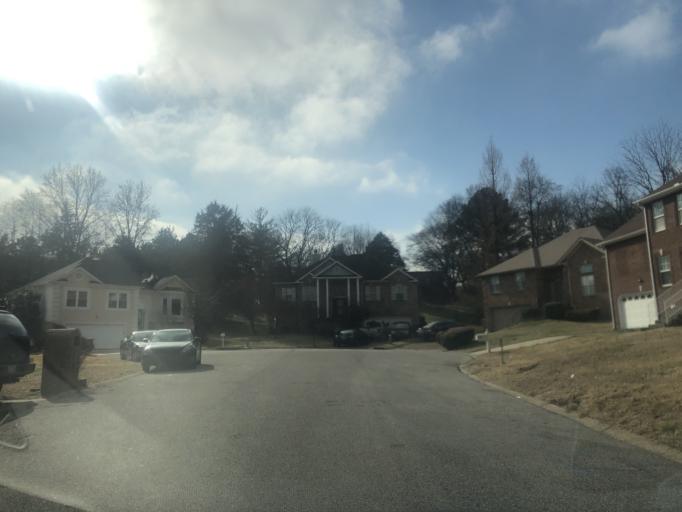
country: US
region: Tennessee
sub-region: Rutherford County
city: La Vergne
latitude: 36.0823
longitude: -86.6529
